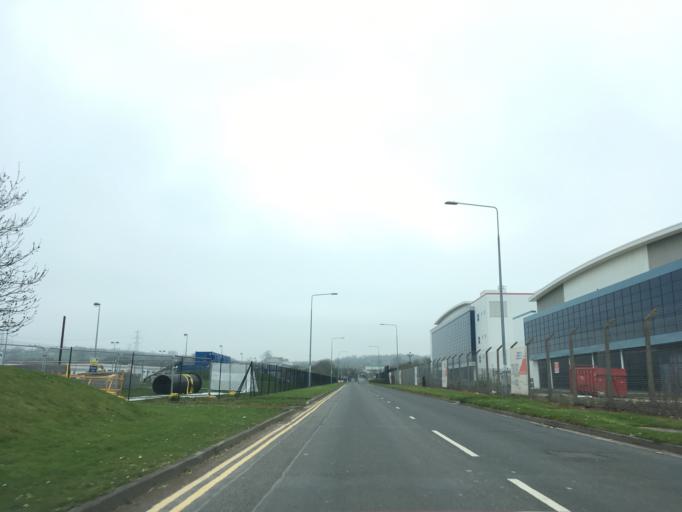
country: GB
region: Wales
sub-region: Newport
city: Marshfield
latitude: 51.5531
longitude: -3.0370
